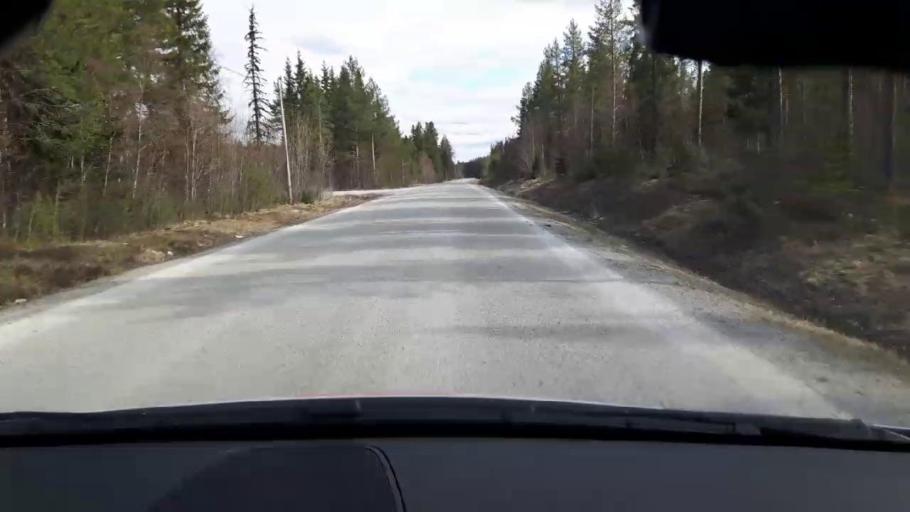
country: SE
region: Jaemtland
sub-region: Bergs Kommun
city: Hoverberg
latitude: 62.7488
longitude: 14.5764
